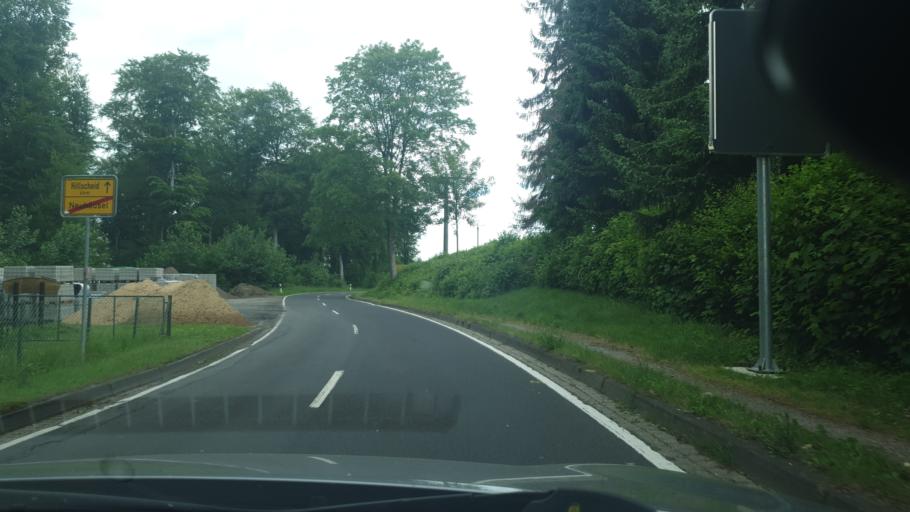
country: DE
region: Rheinland-Pfalz
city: Neuhausel
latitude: 50.3883
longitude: 7.7098
